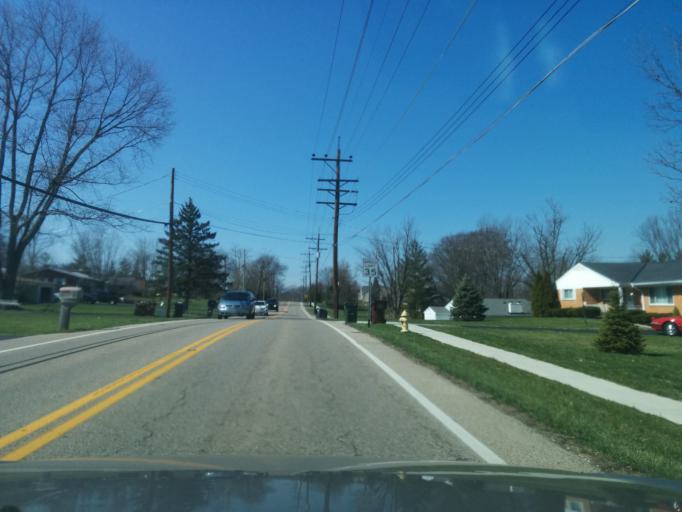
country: US
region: Ohio
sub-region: Hamilton County
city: Northgate
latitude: 39.2361
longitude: -84.6104
